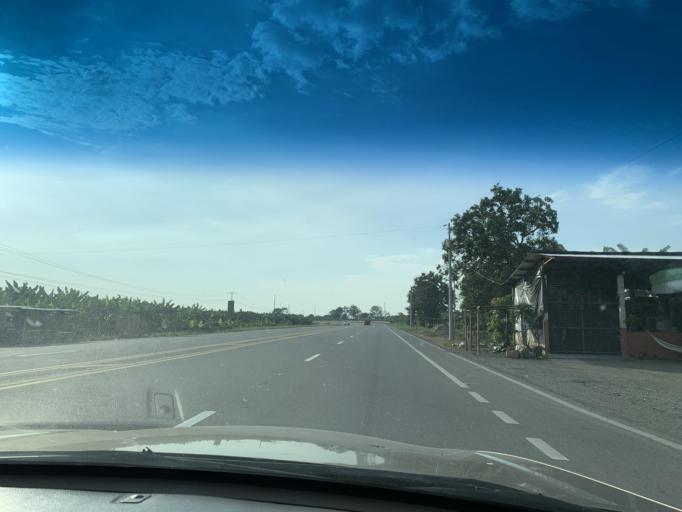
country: EC
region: Guayas
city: Naranjito
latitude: -2.2613
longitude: -79.5494
